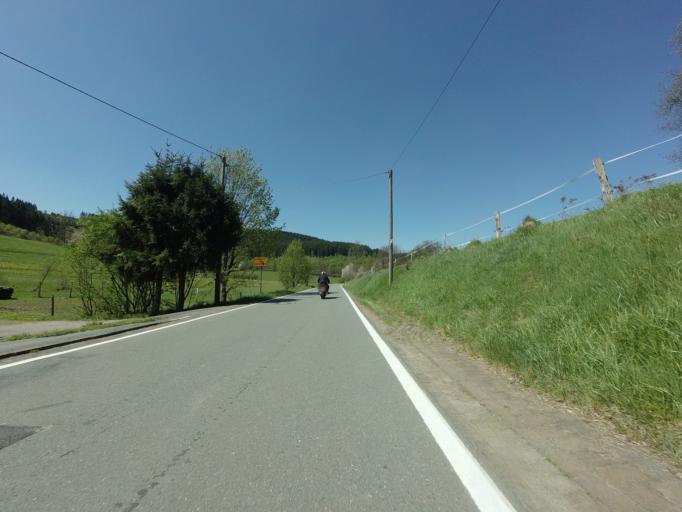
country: DE
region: North Rhine-Westphalia
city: Hilchenbach
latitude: 50.9598
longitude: 8.1123
